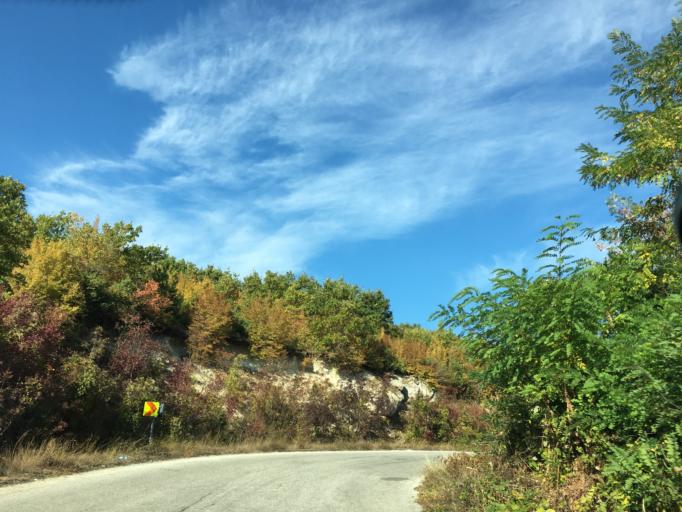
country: BG
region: Khaskovo
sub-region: Obshtina Ivaylovgrad
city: Ivaylovgrad
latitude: 41.4523
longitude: 26.1343
